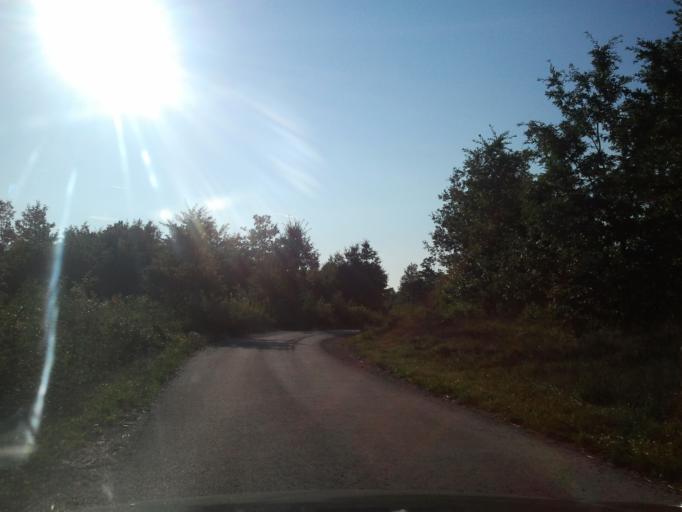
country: HR
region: Zadarska
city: Gracac
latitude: 44.3849
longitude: 15.6970
